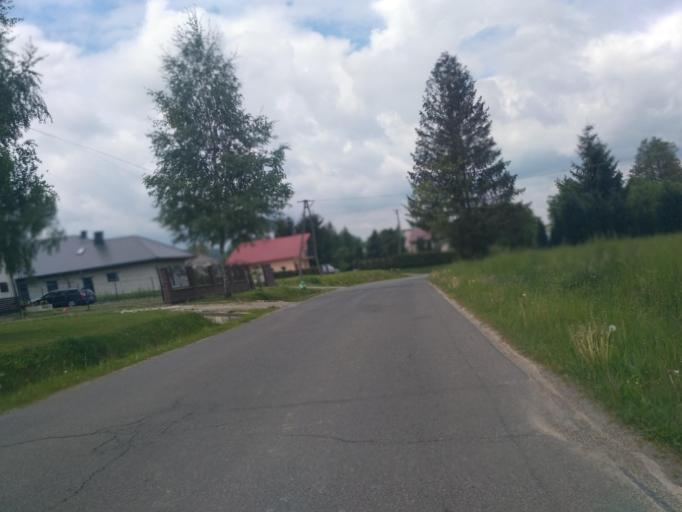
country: PL
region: Subcarpathian Voivodeship
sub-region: Powiat krosnienski
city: Chorkowka
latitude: 49.6650
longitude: 21.6191
